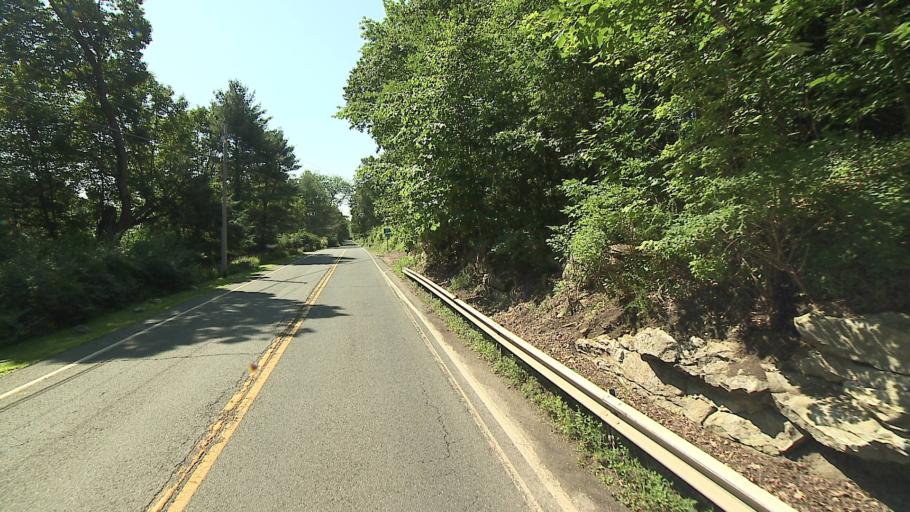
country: US
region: Massachusetts
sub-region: Berkshire County
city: Sheffield
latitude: 42.0497
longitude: -73.4260
